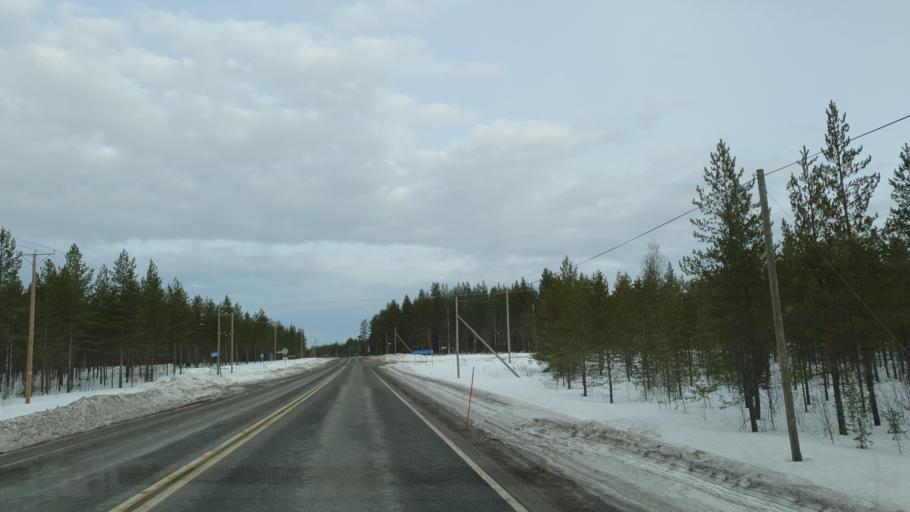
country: FI
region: Kainuu
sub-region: Kajaani
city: Vuokatti
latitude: 64.2144
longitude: 28.1306
